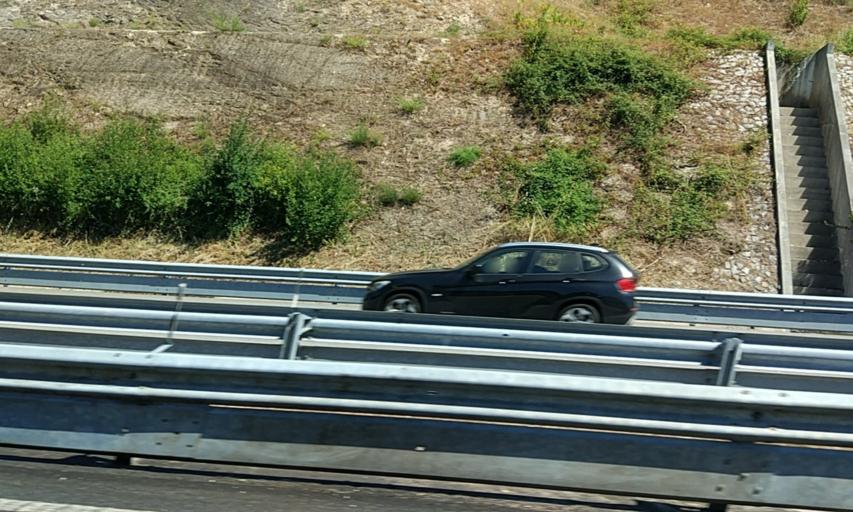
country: PT
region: Porto
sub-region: Amarante
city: Amarante
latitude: 41.2597
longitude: -8.0427
